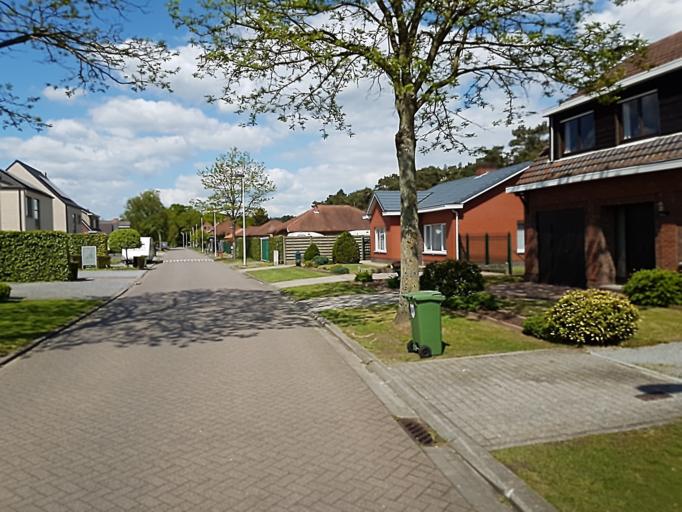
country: BE
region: Flanders
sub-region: Provincie Antwerpen
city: Schilde
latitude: 51.2126
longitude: 4.6071
